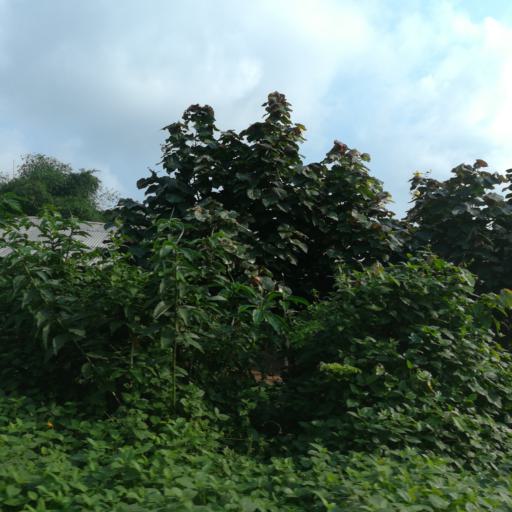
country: NG
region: Rivers
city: Okrika
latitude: 4.7817
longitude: 7.1448
